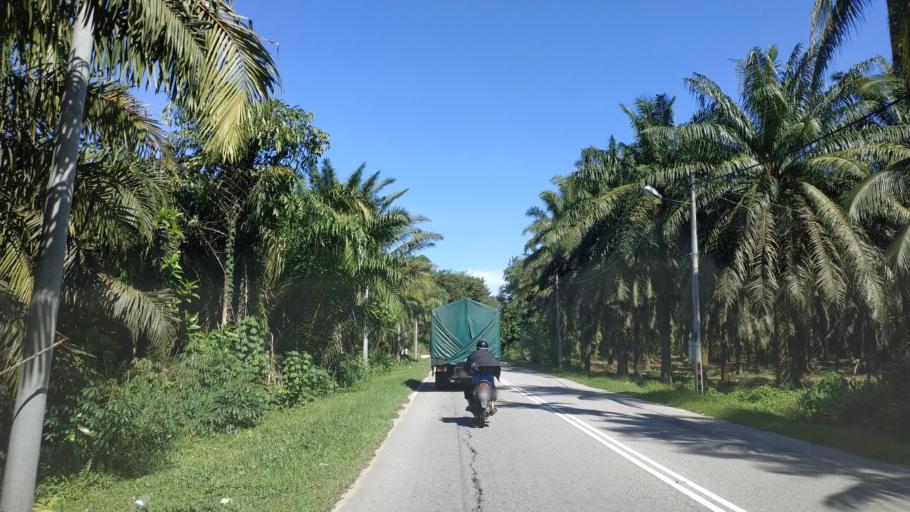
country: MY
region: Kedah
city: Kulim
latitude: 5.3094
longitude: 100.5405
